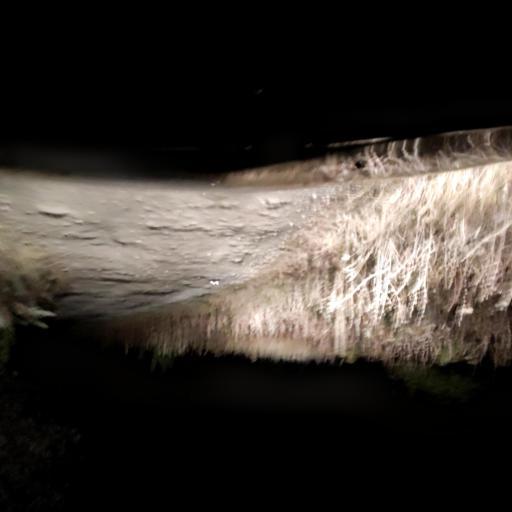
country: RU
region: Voronezj
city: Semiluki
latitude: 51.7202
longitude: 38.9949
